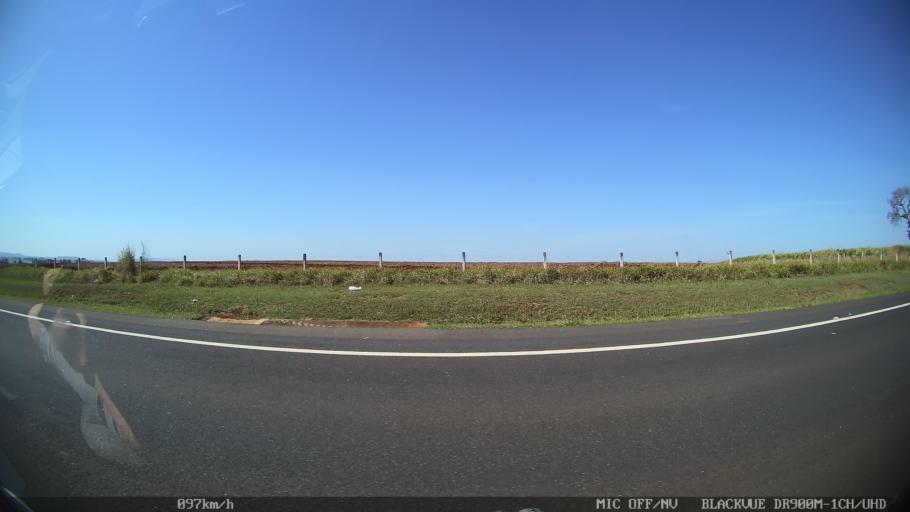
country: BR
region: Sao Paulo
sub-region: Batatais
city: Batatais
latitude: -20.7642
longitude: -47.5342
